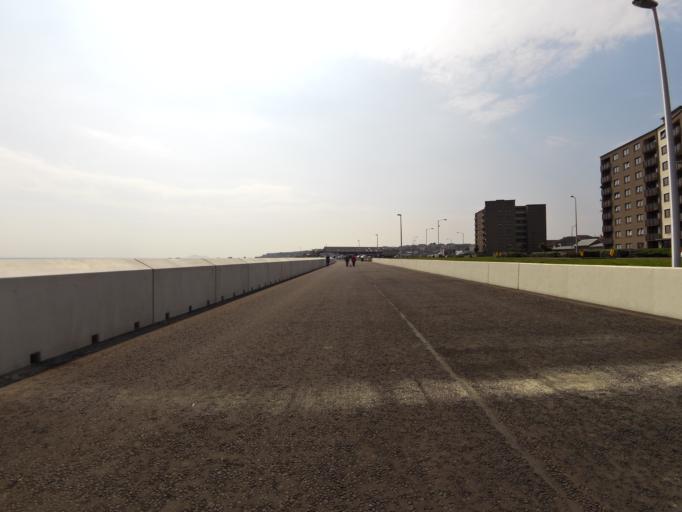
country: GB
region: Scotland
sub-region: Fife
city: Kirkcaldy
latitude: 56.1016
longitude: -3.1596
